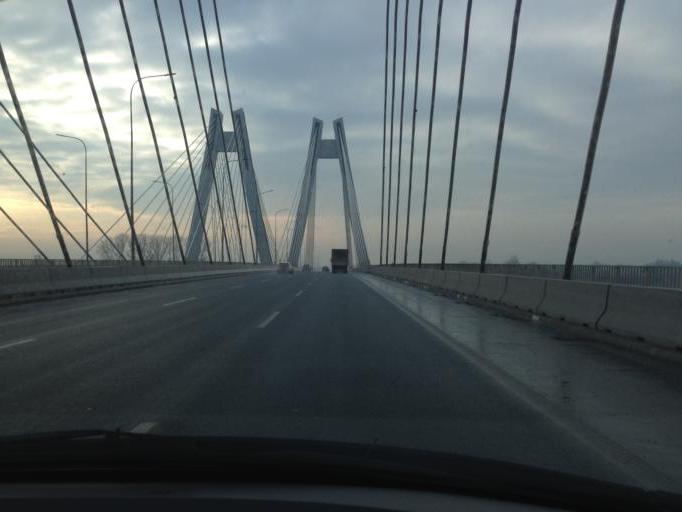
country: PL
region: Lesser Poland Voivodeship
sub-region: Powiat wielicki
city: Kokotow
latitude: 50.0526
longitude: 20.0729
